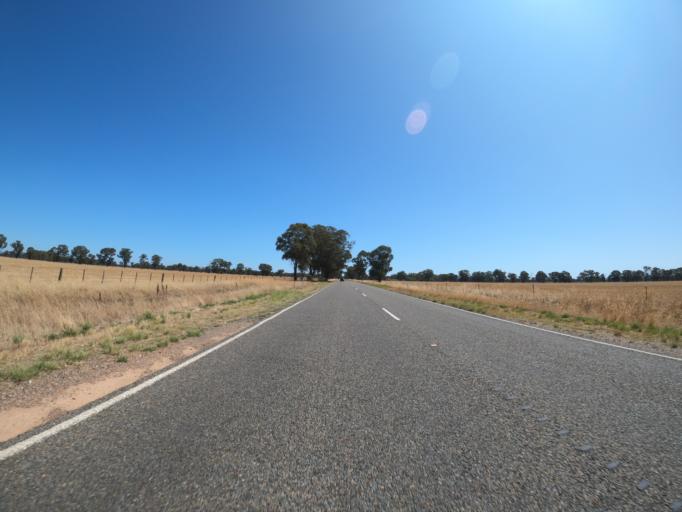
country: AU
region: New South Wales
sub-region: Corowa Shire
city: Corowa
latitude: -36.0734
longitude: 146.3510
